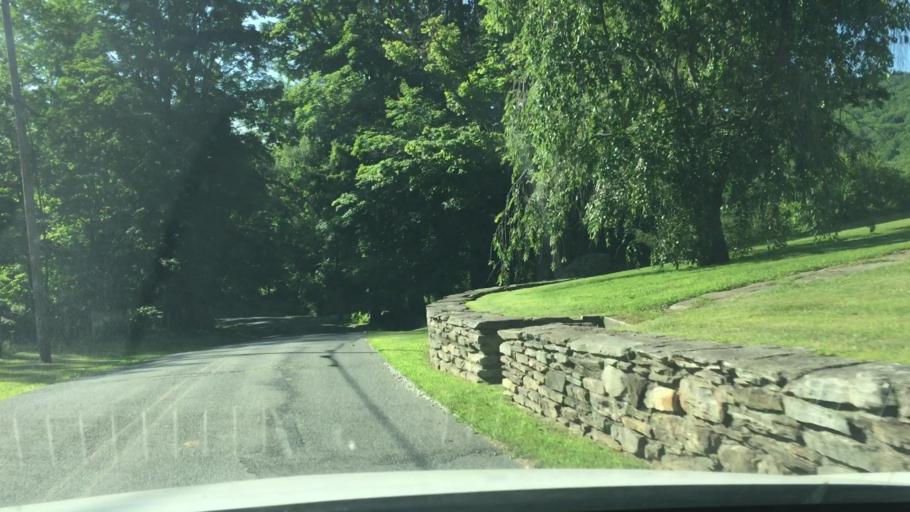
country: US
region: Massachusetts
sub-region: Berkshire County
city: Lee
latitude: 42.2360
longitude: -73.2144
